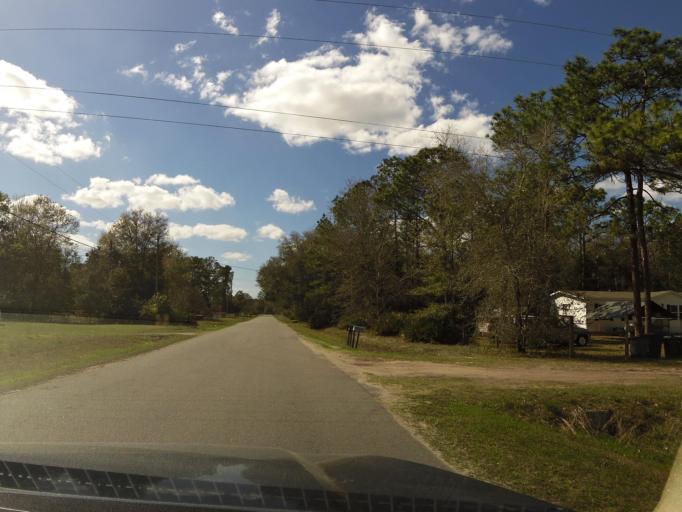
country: US
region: Florida
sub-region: Clay County
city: Middleburg
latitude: 30.1151
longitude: -81.9567
